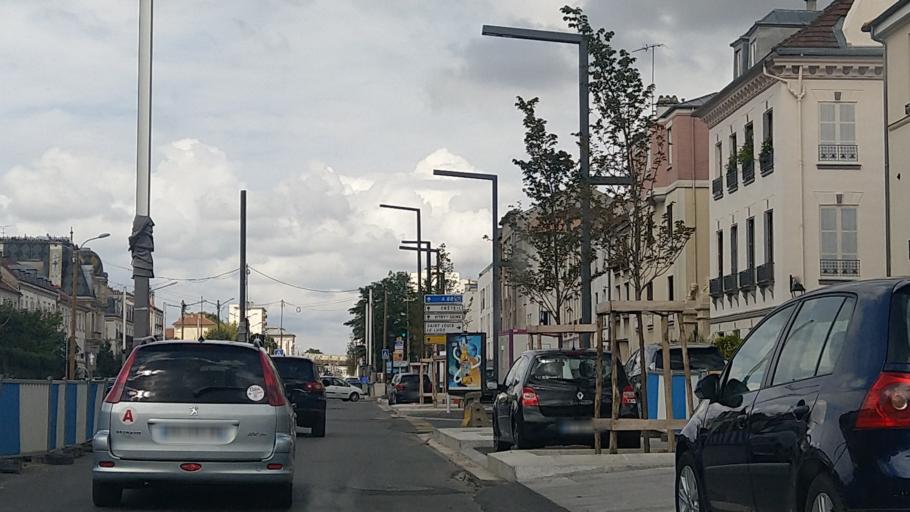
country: FR
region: Ile-de-France
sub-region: Departement du Val-de-Marne
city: Thiais
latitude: 48.7661
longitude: 2.4046
